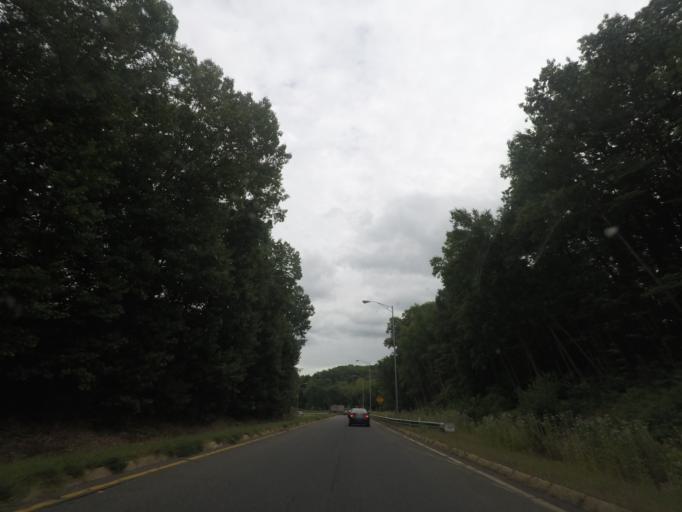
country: US
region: Massachusetts
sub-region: Hampden County
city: Chicopee
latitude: 42.1528
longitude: -72.6411
